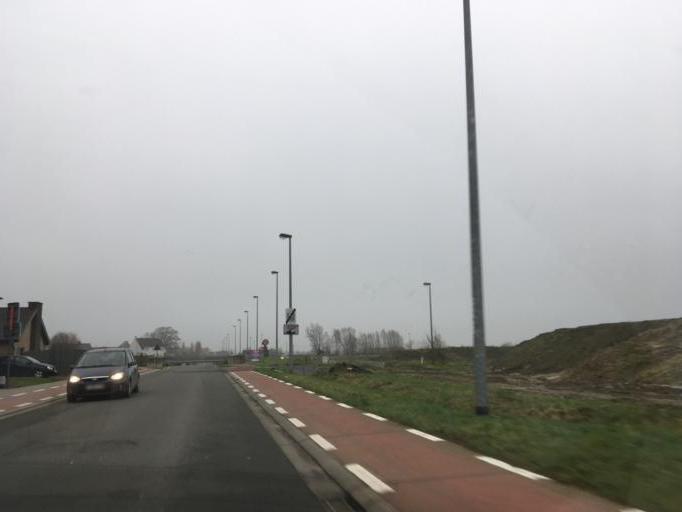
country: BE
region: Flanders
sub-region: Provincie West-Vlaanderen
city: Roeselare
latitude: 50.9776
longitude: 3.1487
